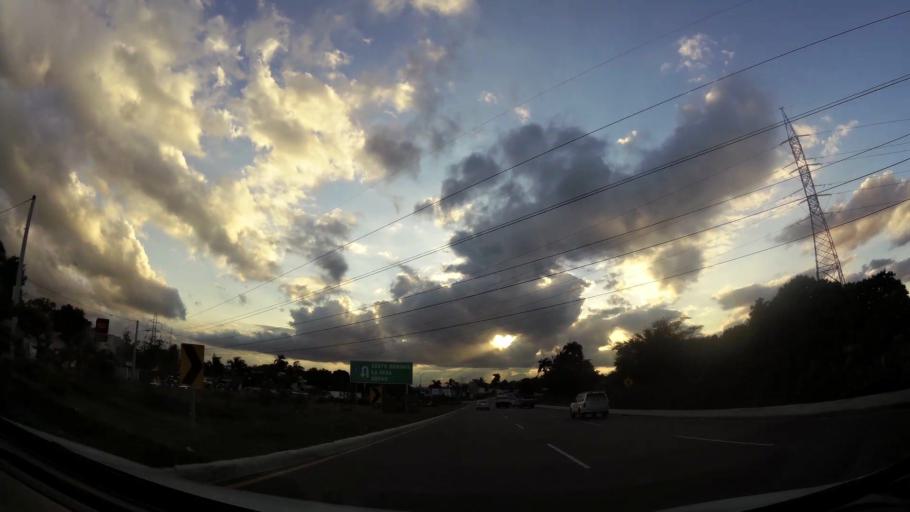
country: DO
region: Santiago
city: Licey al Medio
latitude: 19.4130
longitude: -70.6458
